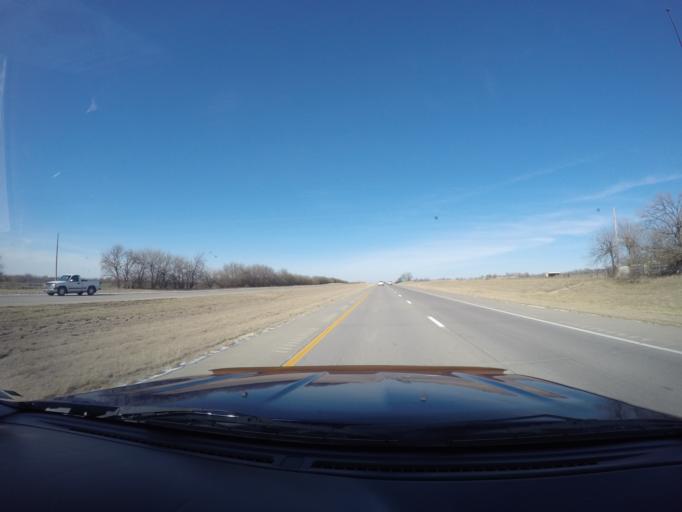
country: US
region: Kansas
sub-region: Sedgwick County
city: Valley Center
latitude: 37.8972
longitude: -97.3264
